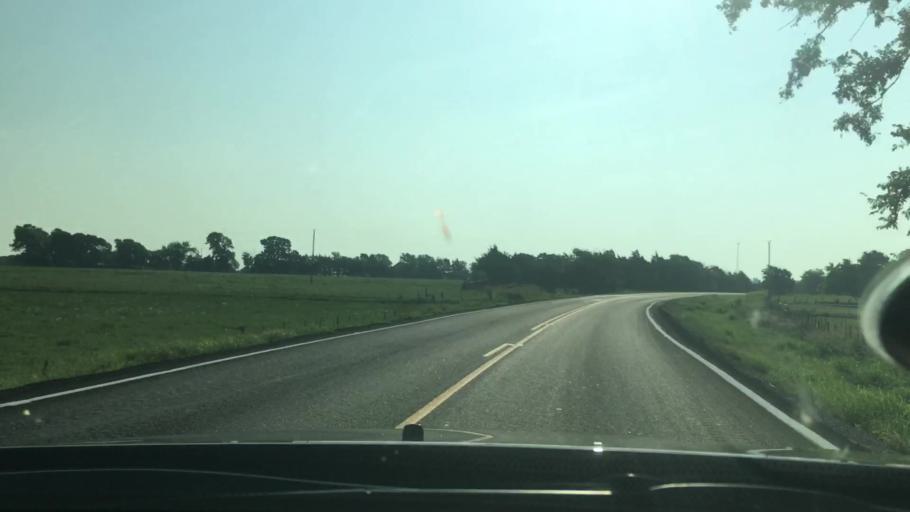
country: US
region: Oklahoma
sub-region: Bryan County
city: Durant
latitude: 34.1425
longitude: -96.2860
